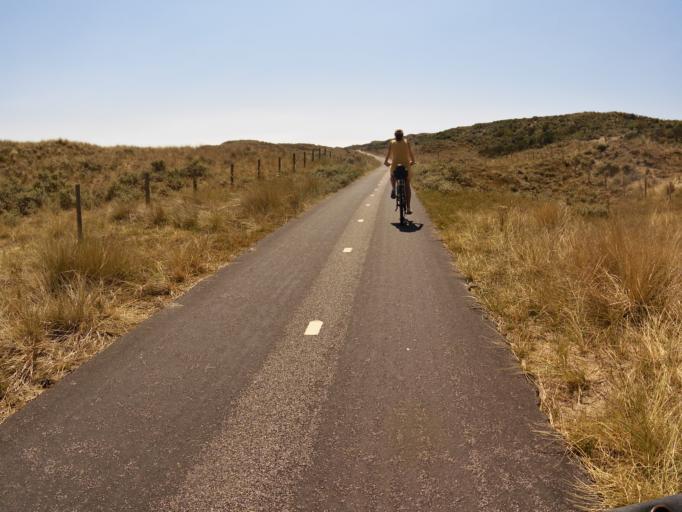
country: NL
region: North Holland
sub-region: Gemeente Zandvoort
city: Zandvoort
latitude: 52.3440
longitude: 4.5080
